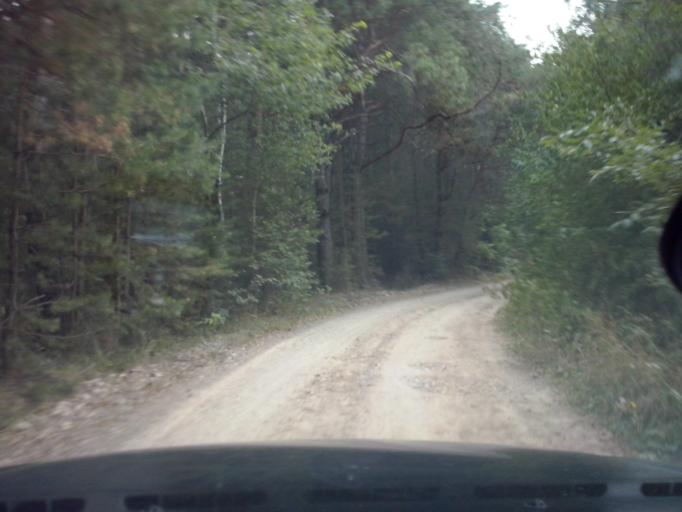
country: PL
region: Swietokrzyskie
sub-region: Kielce
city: Osiedle-Nowiny
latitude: 50.7846
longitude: 20.5381
